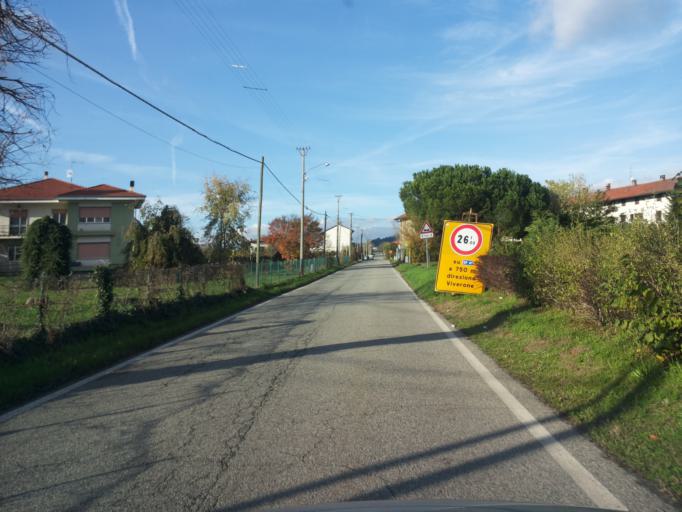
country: IT
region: Piedmont
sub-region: Provincia di Vercelli
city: Alice Castello
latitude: 45.3735
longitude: 8.0736
